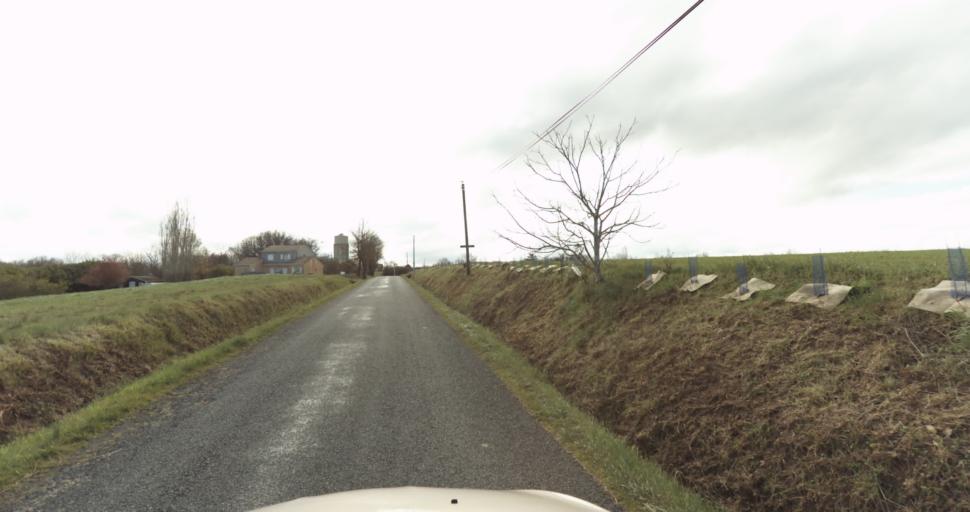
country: FR
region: Midi-Pyrenees
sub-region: Departement du Tarn
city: Frejairolles
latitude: 43.8676
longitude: 2.2031
